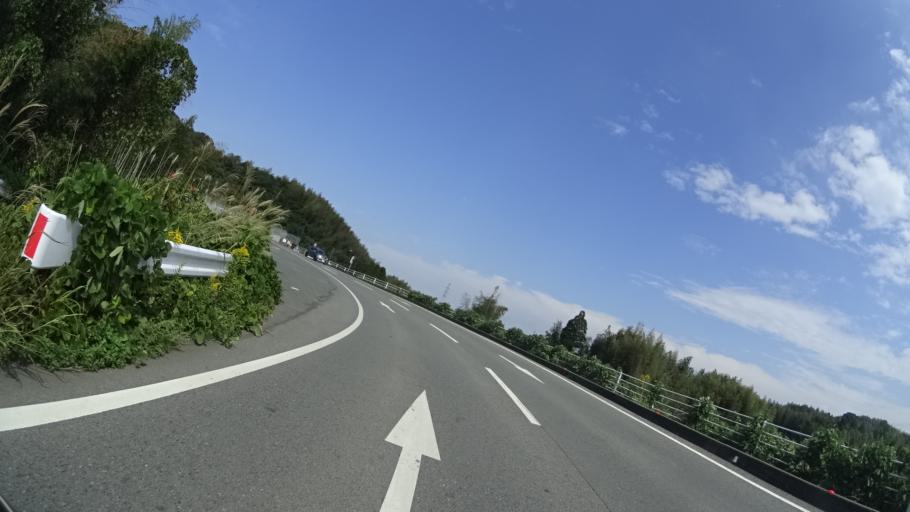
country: JP
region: Kumamoto
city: Uto
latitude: 32.6752
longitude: 130.7214
